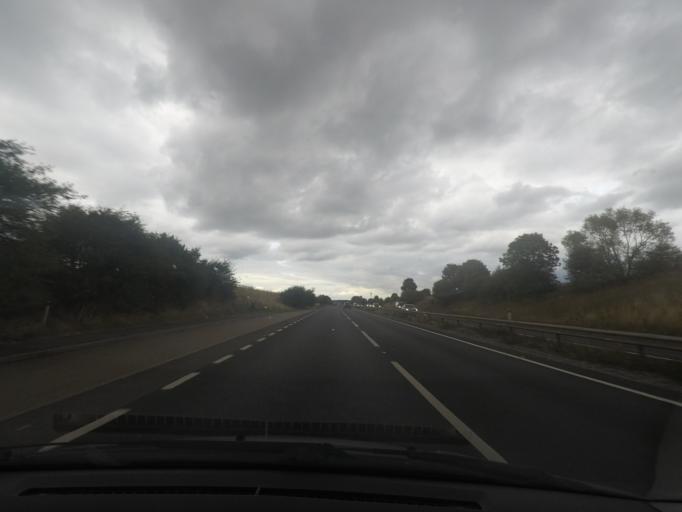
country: GB
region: England
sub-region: Oxfordshire
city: Marcham
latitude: 51.6509
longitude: -1.3191
